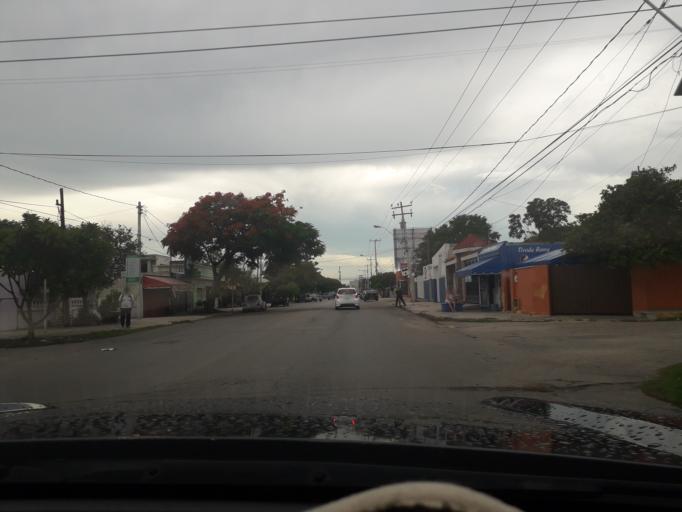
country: MX
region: Yucatan
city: Merida
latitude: 20.9552
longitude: -89.6486
